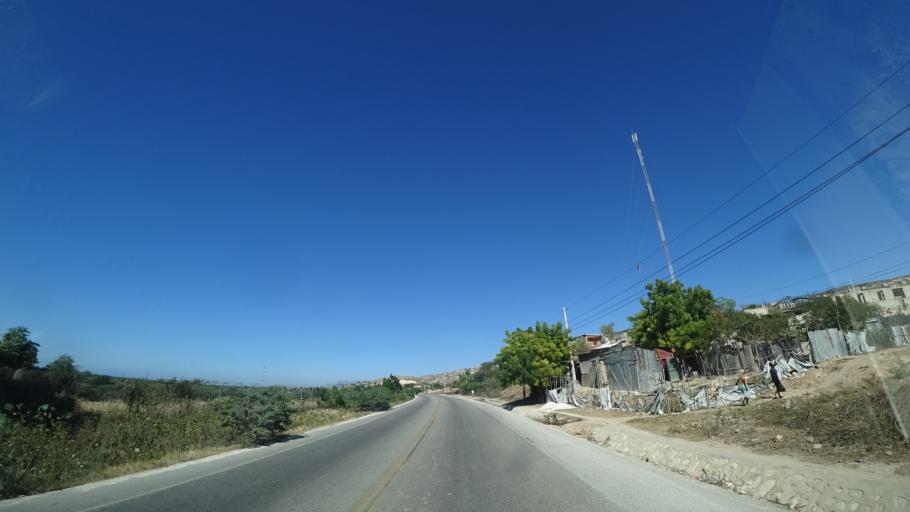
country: HT
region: Ouest
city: Croix des Bouquets
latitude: 18.6560
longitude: -72.2866
